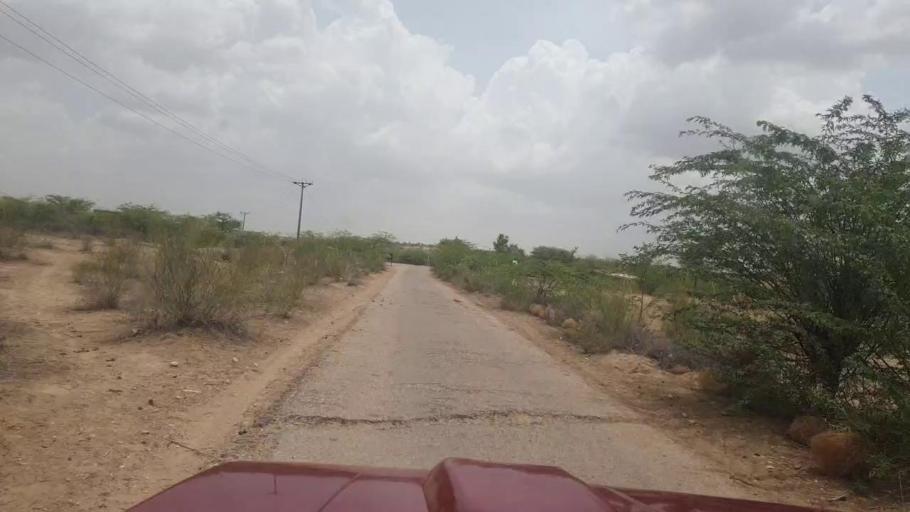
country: PK
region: Sindh
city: Islamkot
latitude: 25.1028
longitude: 70.3709
